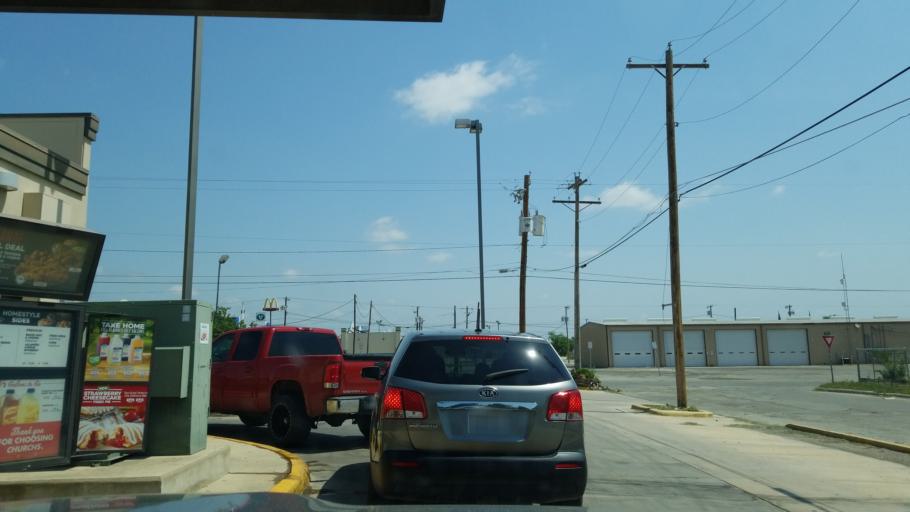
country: US
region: Texas
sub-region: Dimmit County
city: Carrizo Springs
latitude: 28.5217
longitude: -99.8564
